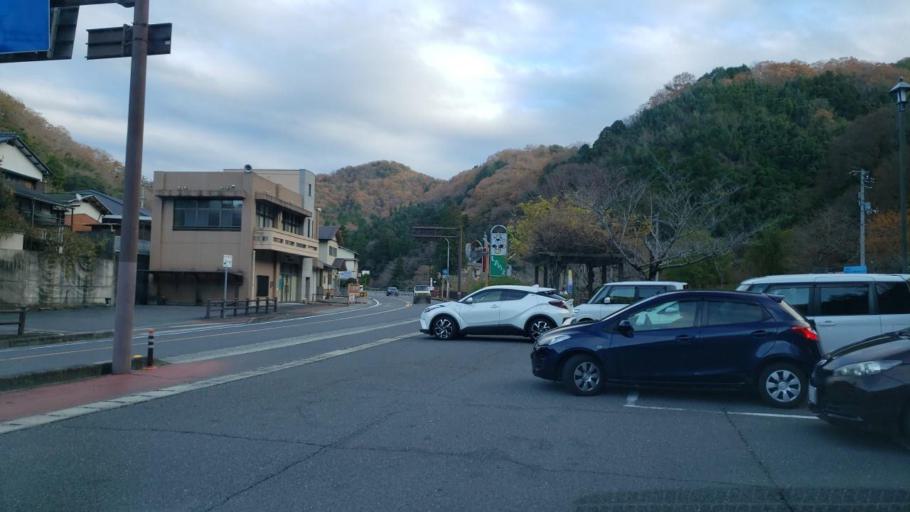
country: JP
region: Tokushima
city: Wakimachi
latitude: 34.1698
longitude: 134.0823
